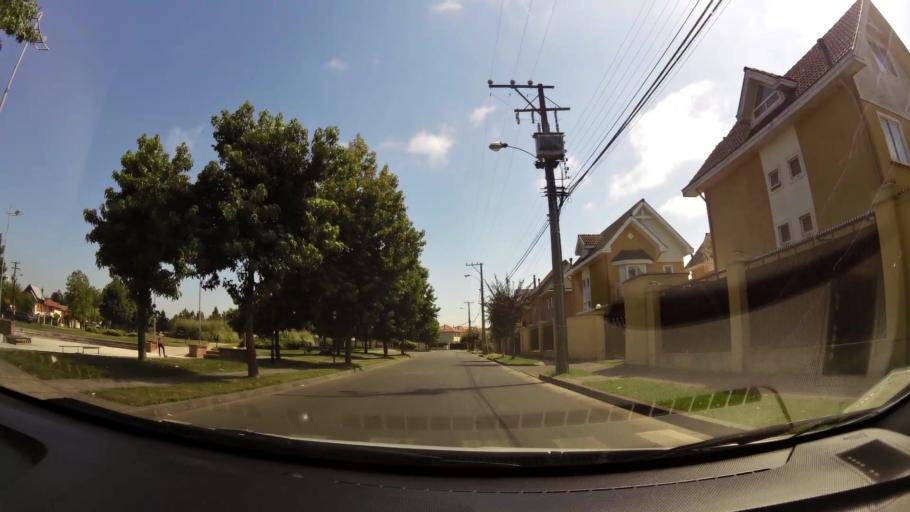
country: CL
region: Biobio
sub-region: Provincia de Concepcion
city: Concepcion
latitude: -36.7768
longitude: -73.0478
